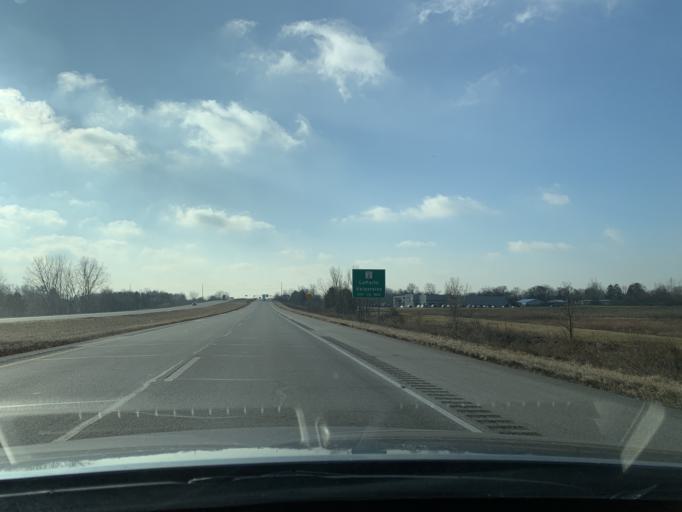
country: US
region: Indiana
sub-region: Porter County
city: Valparaiso
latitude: 41.4821
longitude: -87.0206
